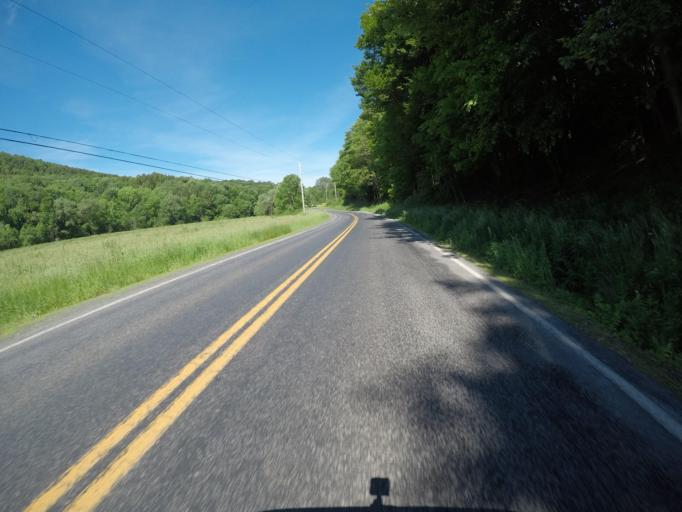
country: US
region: New York
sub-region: Delaware County
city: Delhi
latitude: 42.2013
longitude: -74.9654
